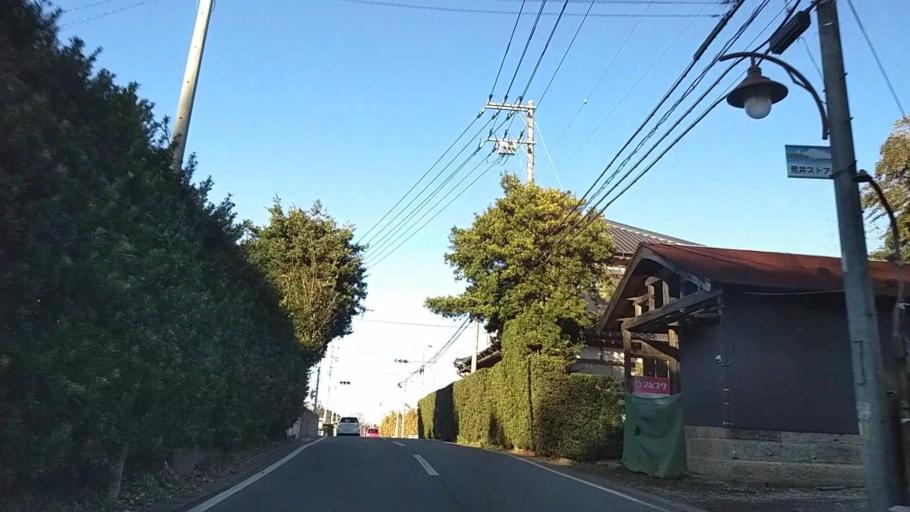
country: JP
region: Chiba
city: Asahi
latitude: 35.7217
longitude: 140.7352
